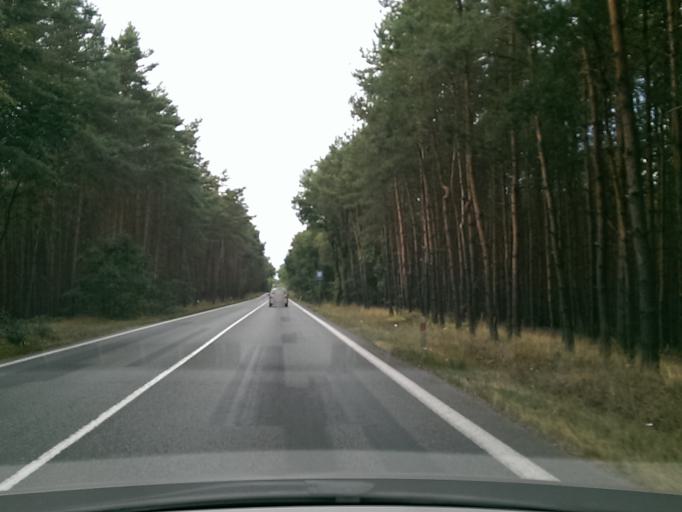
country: CZ
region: Central Bohemia
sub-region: Okres Nymburk
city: Podebrady
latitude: 50.1095
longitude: 15.1355
